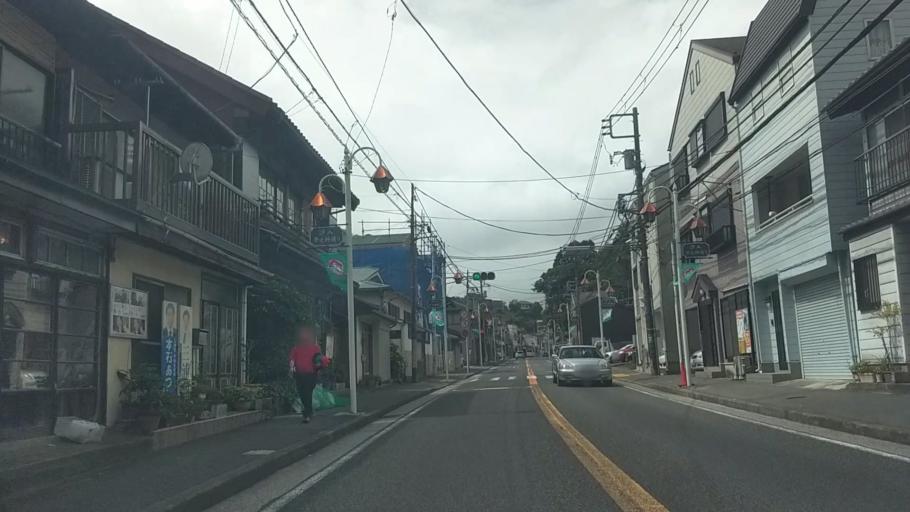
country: JP
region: Kanagawa
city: Yokosuka
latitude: 35.2774
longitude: 139.6608
